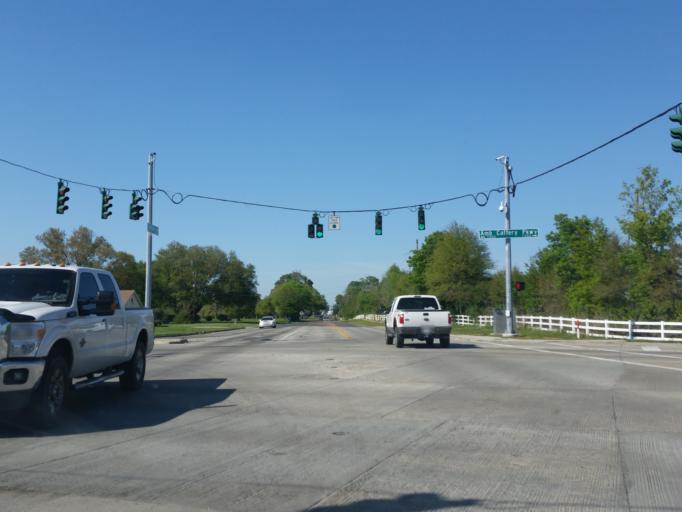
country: US
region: Louisiana
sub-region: Lafayette Parish
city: Broussard
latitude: 30.1318
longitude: -91.9652
